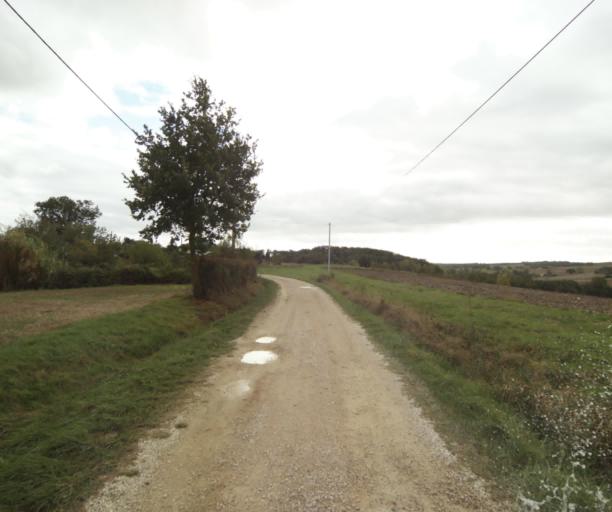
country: FR
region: Midi-Pyrenees
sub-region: Departement du Tarn-et-Garonne
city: Beaumont-de-Lomagne
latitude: 43.9002
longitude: 1.0892
